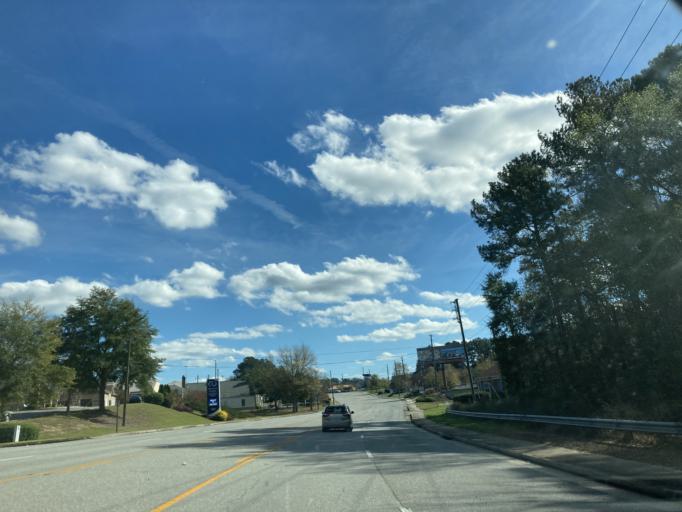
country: US
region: Georgia
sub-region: Bibb County
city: Macon
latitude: 32.8930
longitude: -83.6818
